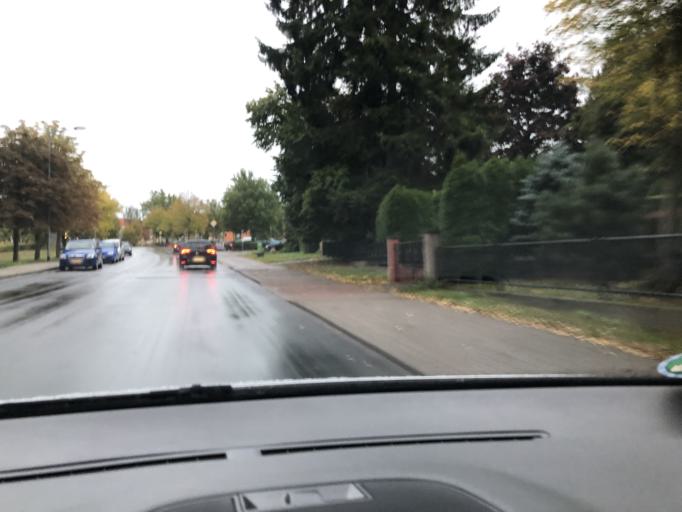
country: DE
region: Thuringia
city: Ilmenau
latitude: 50.6788
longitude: 10.9206
